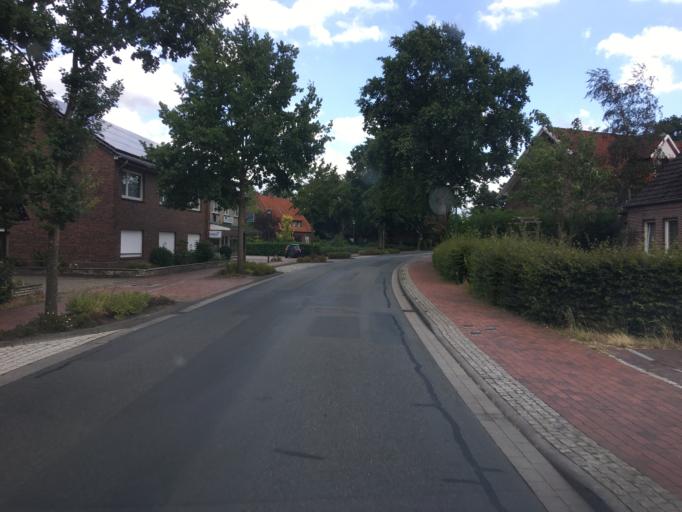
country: DE
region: Lower Saxony
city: Hilkenbrook
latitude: 53.0717
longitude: 7.7014
